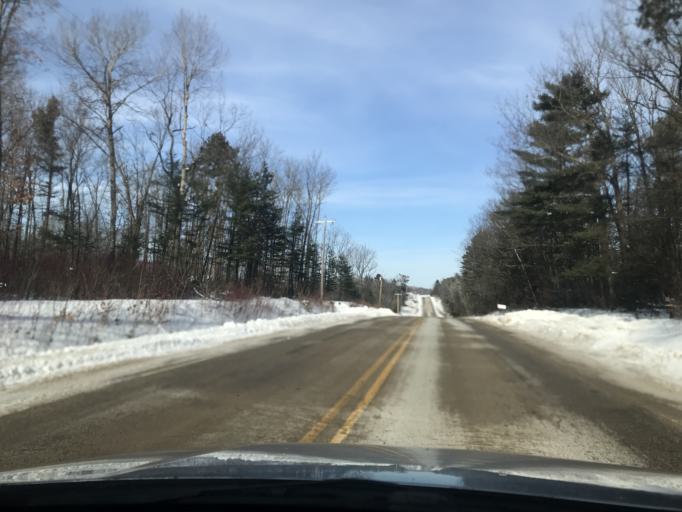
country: US
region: Wisconsin
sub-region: Oconto County
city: Oconto Falls
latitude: 45.1381
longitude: -88.1773
